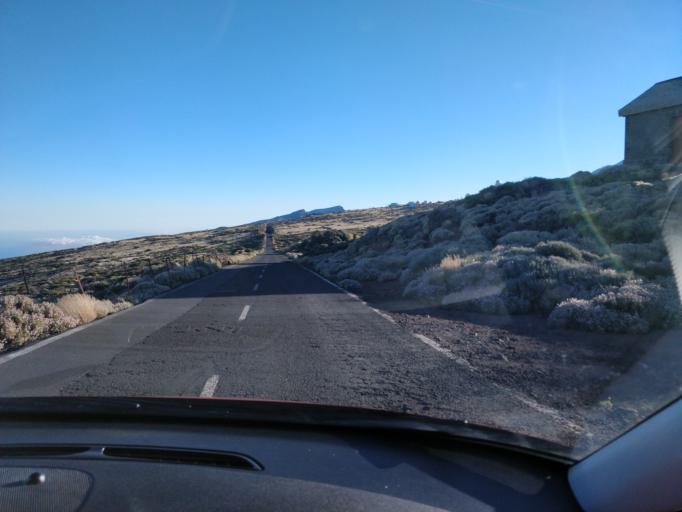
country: ES
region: Canary Islands
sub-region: Provincia de Santa Cruz de Tenerife
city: Guimar
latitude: 28.3066
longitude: -16.5005
